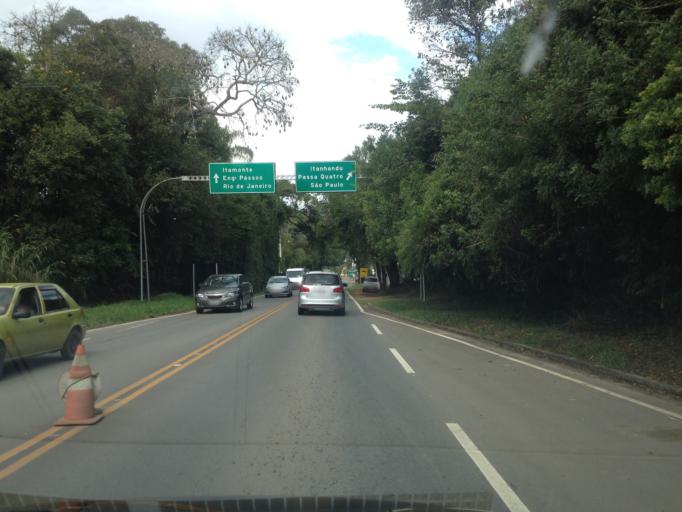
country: BR
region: Minas Gerais
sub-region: Itanhandu
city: Itanhandu
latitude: -22.2459
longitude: -44.9353
